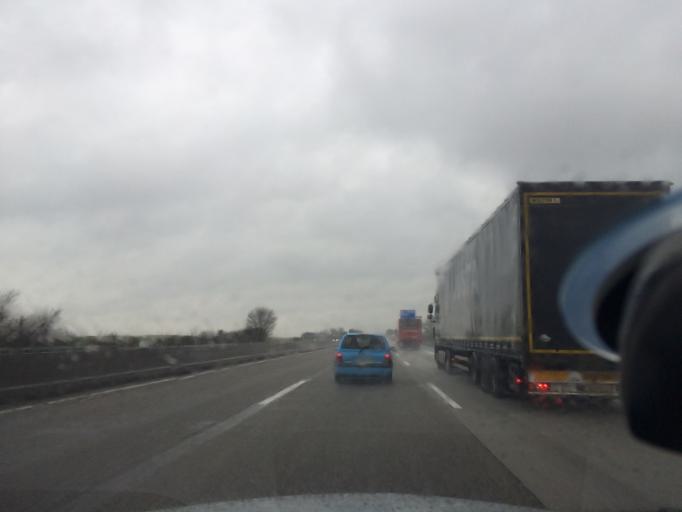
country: DE
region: Hesse
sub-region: Regierungsbezirk Darmstadt
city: Ober-Morlen
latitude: 50.3800
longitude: 8.7054
